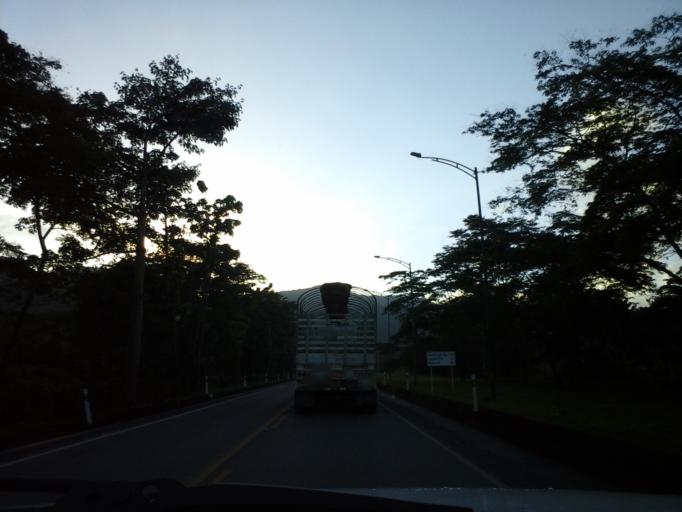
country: CO
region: Meta
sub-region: Villavicencio
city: Villavicencio
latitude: 4.1249
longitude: -73.6493
